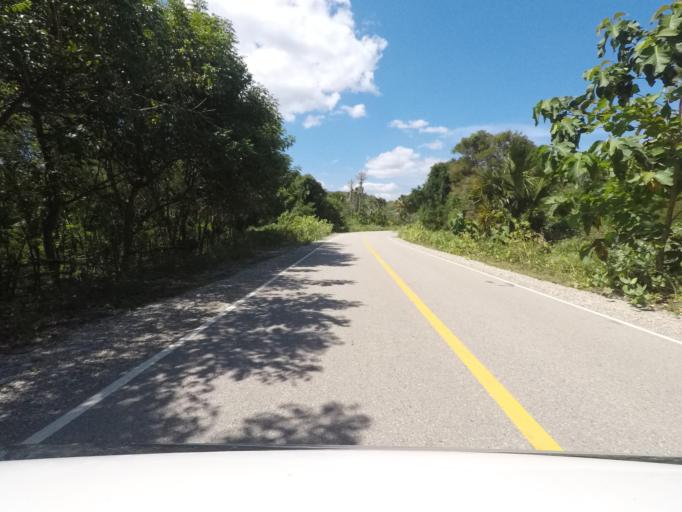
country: TL
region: Lautem
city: Lospalos
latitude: -8.4133
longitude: 126.8069
